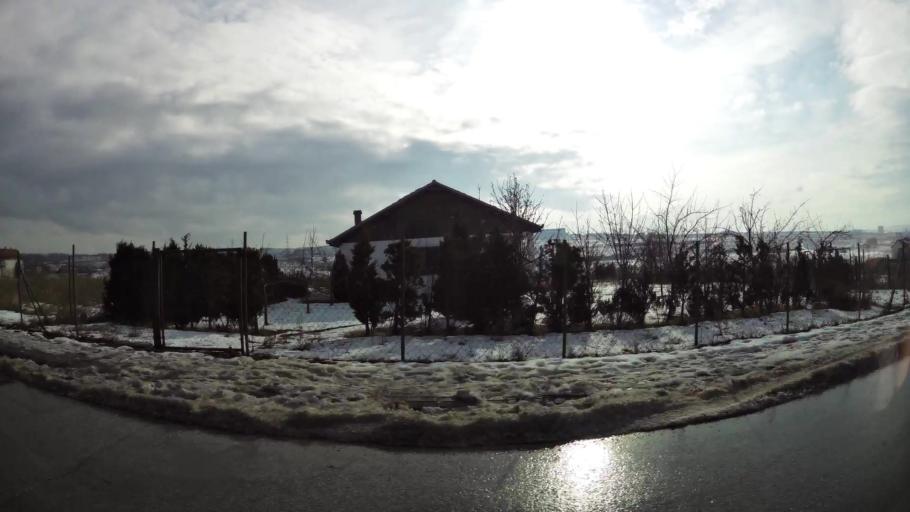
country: XK
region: Pristina
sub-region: Komuna e Prishtines
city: Pristina
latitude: 42.6727
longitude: 21.1427
